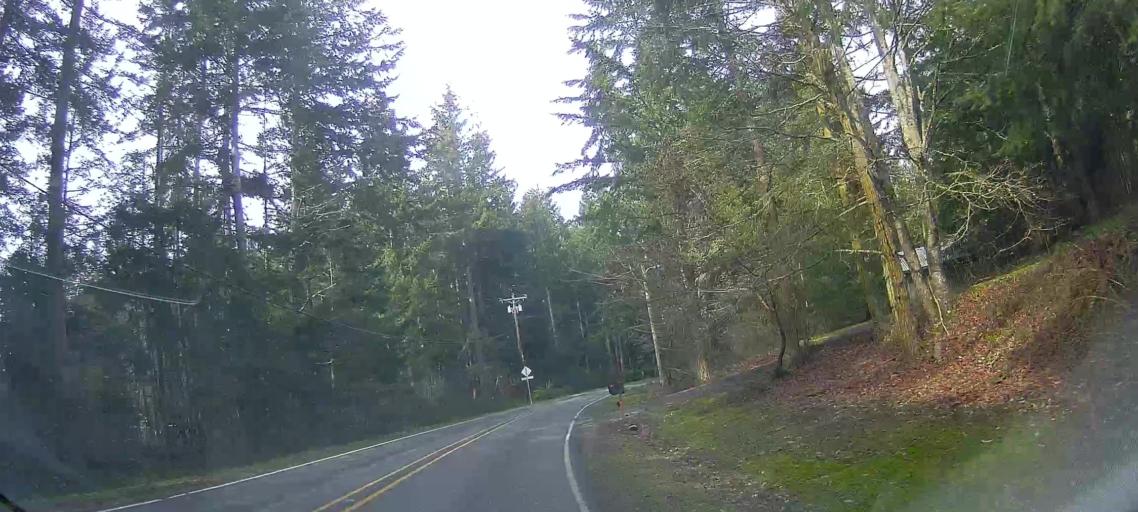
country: US
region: Washington
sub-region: Island County
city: Camano
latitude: 48.2011
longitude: -122.5329
